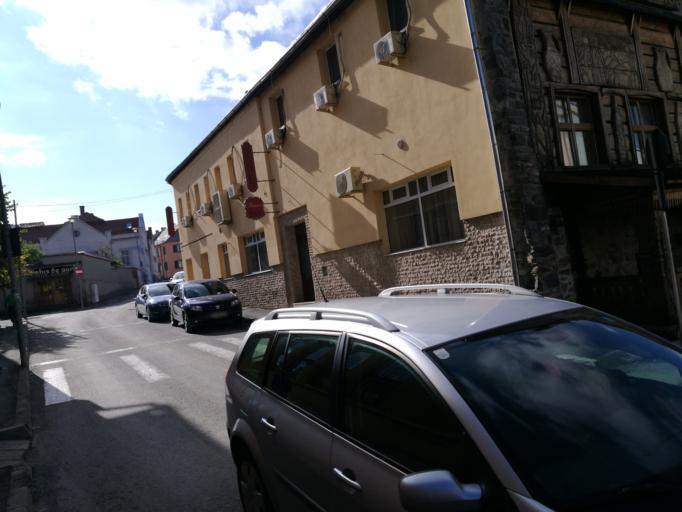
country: RO
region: Sibiu
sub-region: Municipiul Sibiu
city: Sibiu
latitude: 45.7916
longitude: 24.1514
